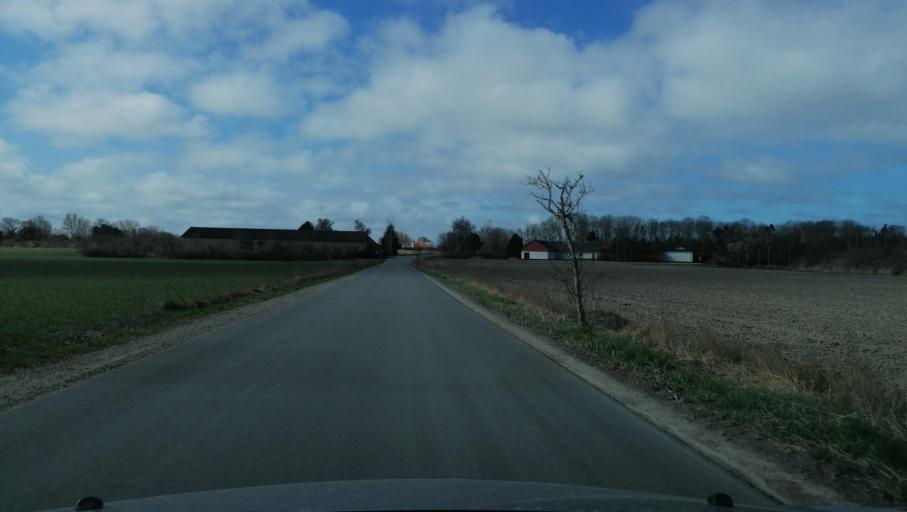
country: DK
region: Zealand
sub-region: Odsherred Kommune
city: Horve
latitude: 55.7762
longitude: 11.4264
